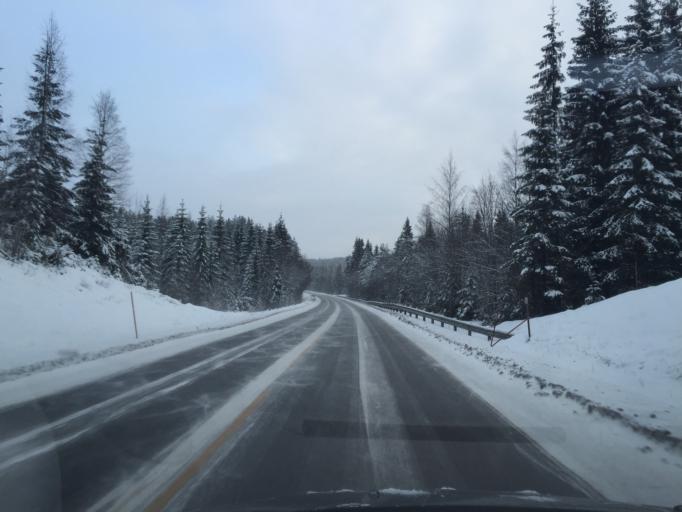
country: NO
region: Hedmark
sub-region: Elverum
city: Elverum
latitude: 60.9477
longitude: 11.6946
